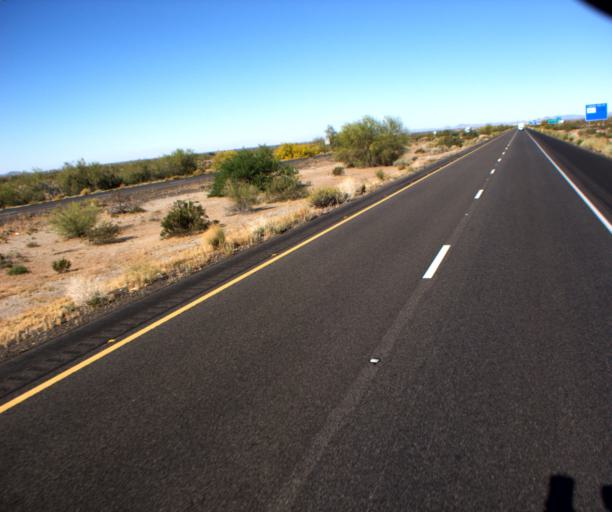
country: US
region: Arizona
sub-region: Maricopa County
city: Gila Bend
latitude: 32.9211
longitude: -112.6514
